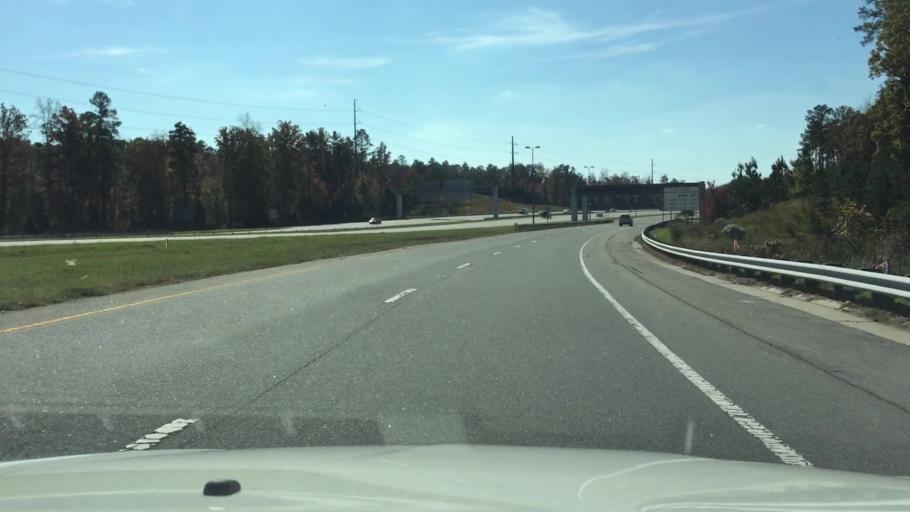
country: US
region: North Carolina
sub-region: Wake County
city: Morrisville
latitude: 35.8514
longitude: -78.8639
